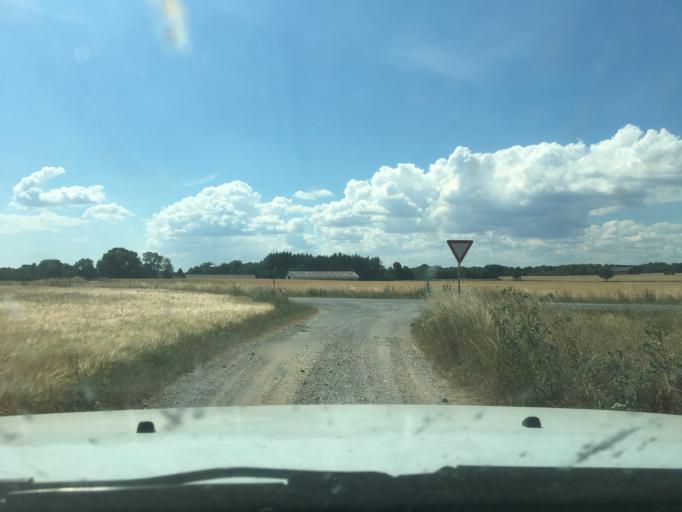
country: DK
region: Central Jutland
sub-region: Arhus Kommune
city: Trige
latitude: 56.3400
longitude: 10.1896
